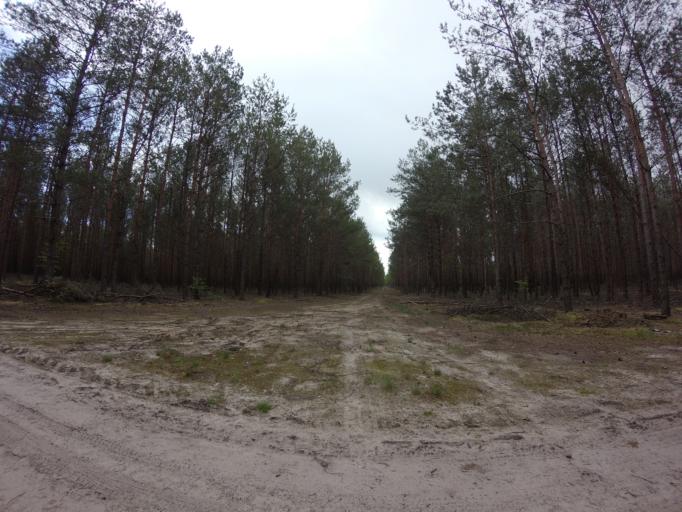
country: PL
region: West Pomeranian Voivodeship
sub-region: Powiat drawski
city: Kalisz Pomorski
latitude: 53.1799
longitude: 15.9712
